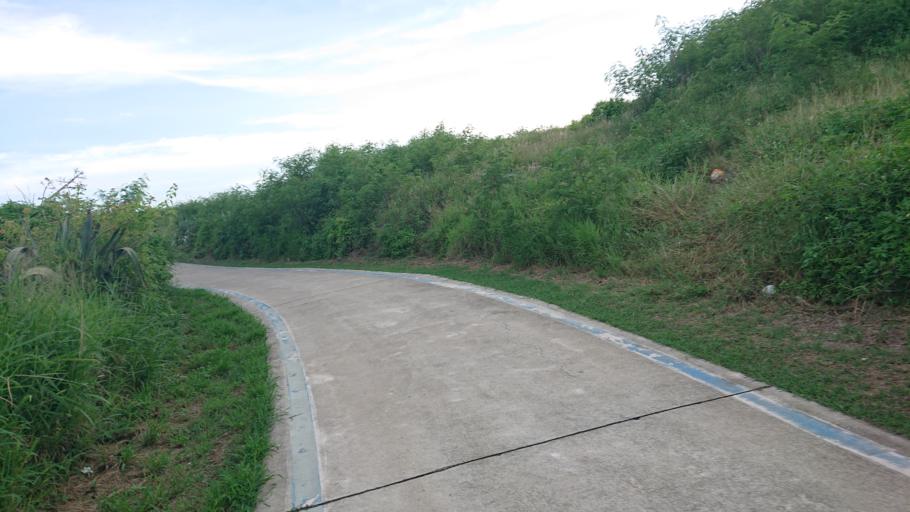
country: TW
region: Taiwan
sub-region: Penghu
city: Ma-kung
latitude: 23.5166
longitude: 119.6053
